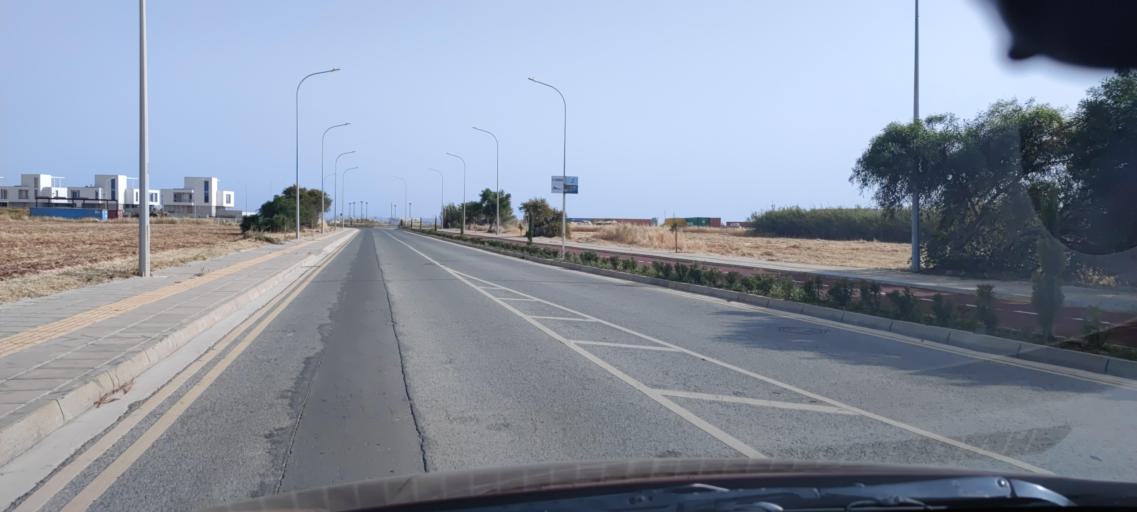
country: CY
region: Ammochostos
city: Liopetri
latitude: 34.9814
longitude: 33.9392
